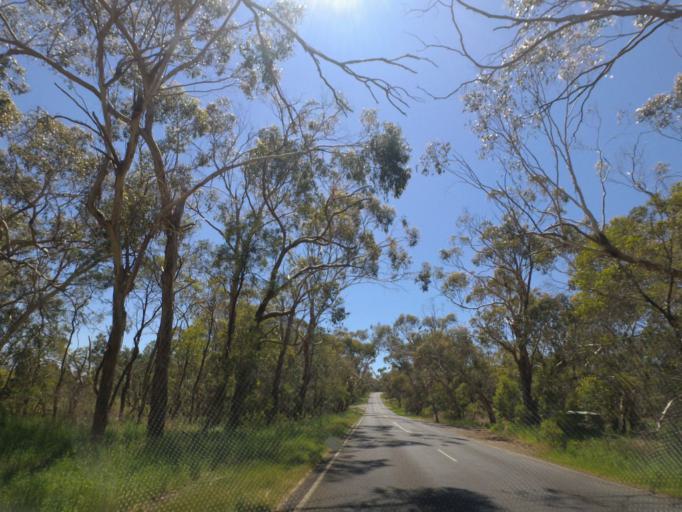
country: AU
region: Victoria
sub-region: Melton
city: Melton West
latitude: -37.5106
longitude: 144.5660
